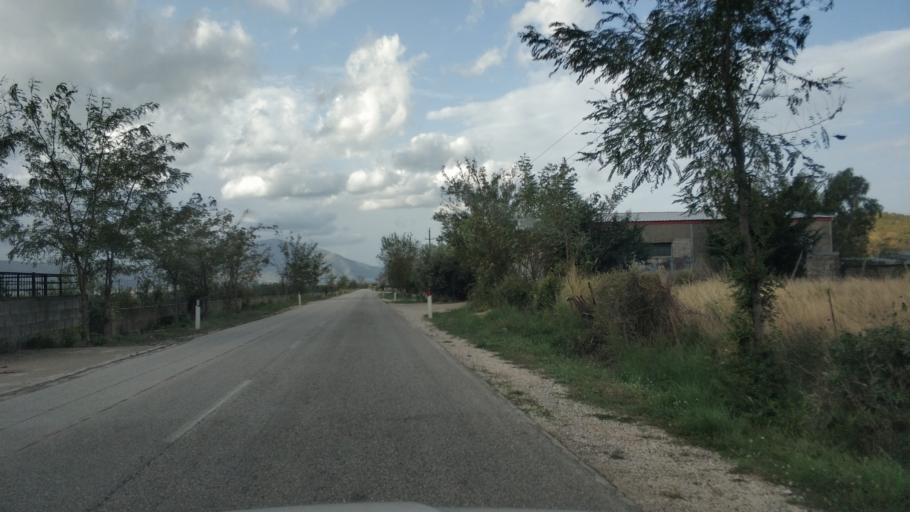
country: AL
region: Vlore
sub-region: Rrethi i Vlores
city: Orikum
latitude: 40.2851
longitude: 19.4973
